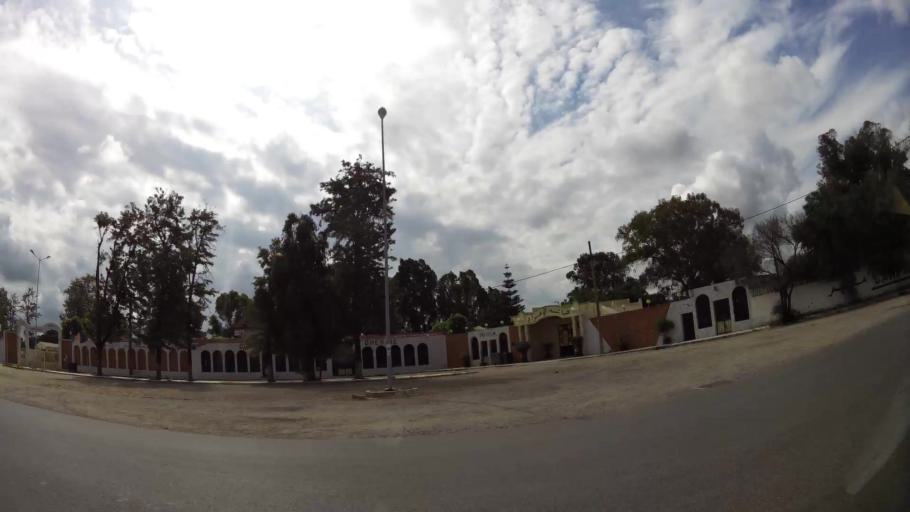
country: MA
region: Gharb-Chrarda-Beni Hssen
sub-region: Kenitra Province
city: Kenitra
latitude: 34.2565
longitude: -6.5684
